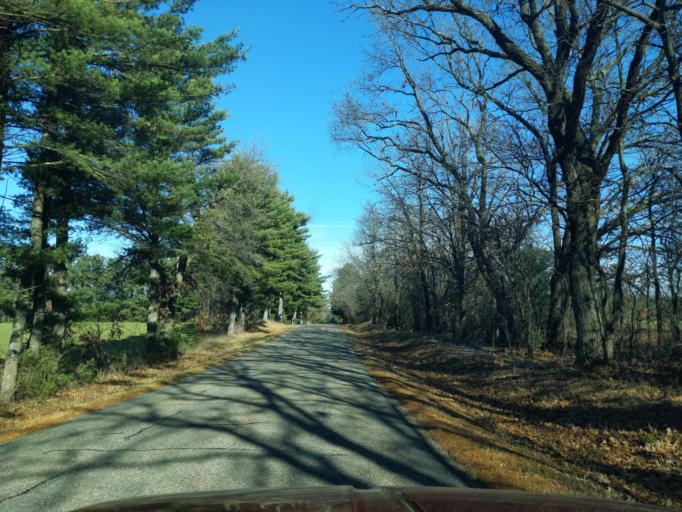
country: US
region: Wisconsin
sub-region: Waushara County
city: Silver Lake
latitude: 44.0782
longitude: -89.1940
